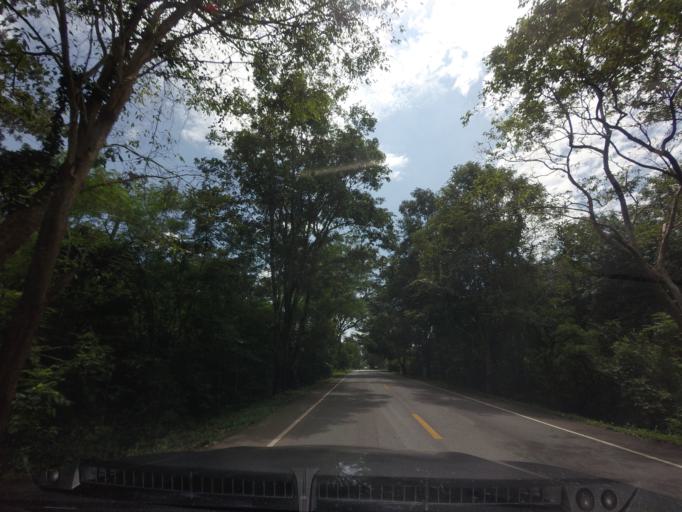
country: TH
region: Nong Khai
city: Pho Tak
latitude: 17.8009
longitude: 102.3472
